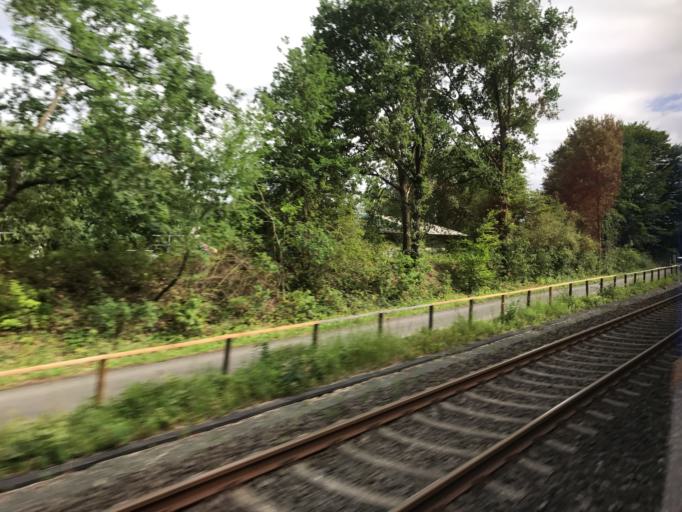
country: DE
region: Hesse
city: Leun
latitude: 50.5394
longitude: 8.3793
